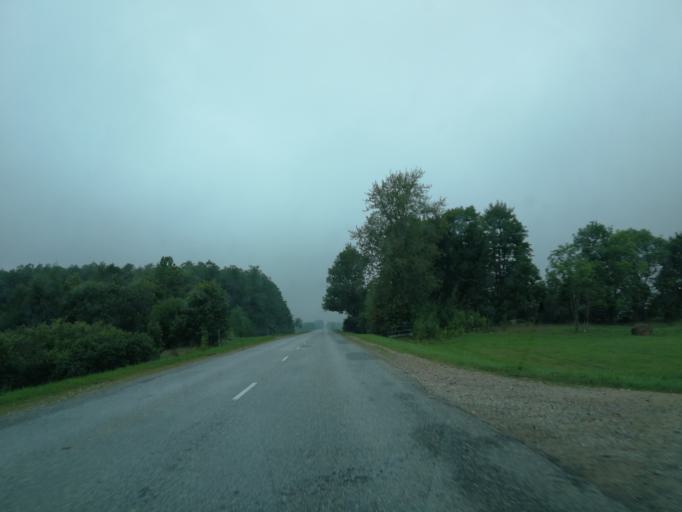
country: LV
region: Varkava
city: Vecvarkava
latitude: 56.3101
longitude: 26.5638
